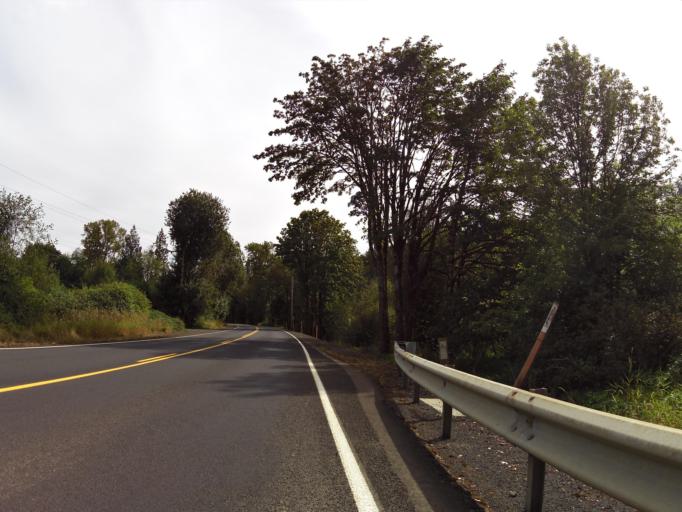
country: US
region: Washington
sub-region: Cowlitz County
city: Castle Rock
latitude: 46.3377
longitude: -122.9364
